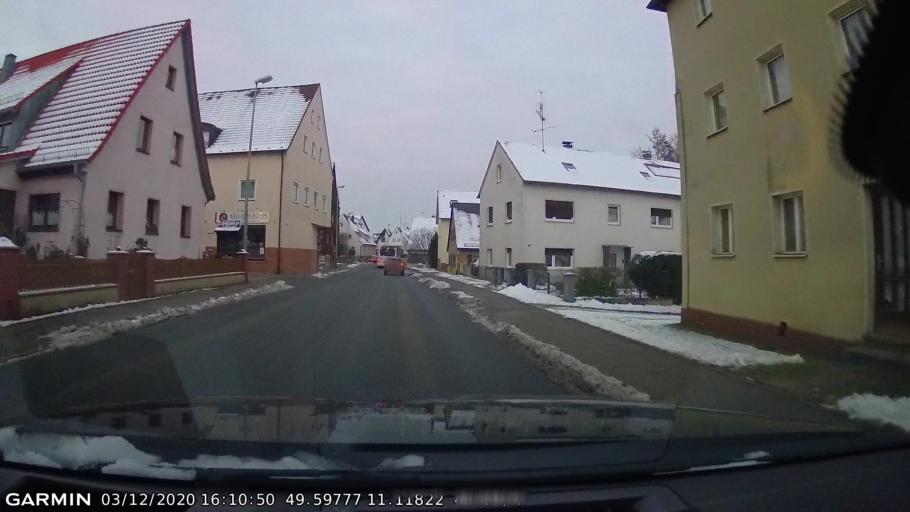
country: DE
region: Bavaria
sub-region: Upper Franconia
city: Dormitz
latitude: 49.5977
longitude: 11.1184
